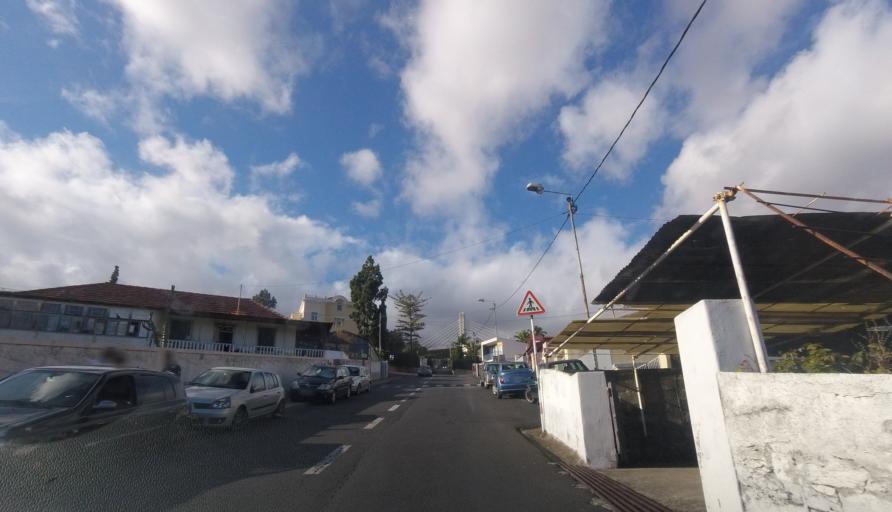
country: PT
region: Madeira
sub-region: Funchal
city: Nossa Senhora do Monte
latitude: 32.6602
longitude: -16.9084
